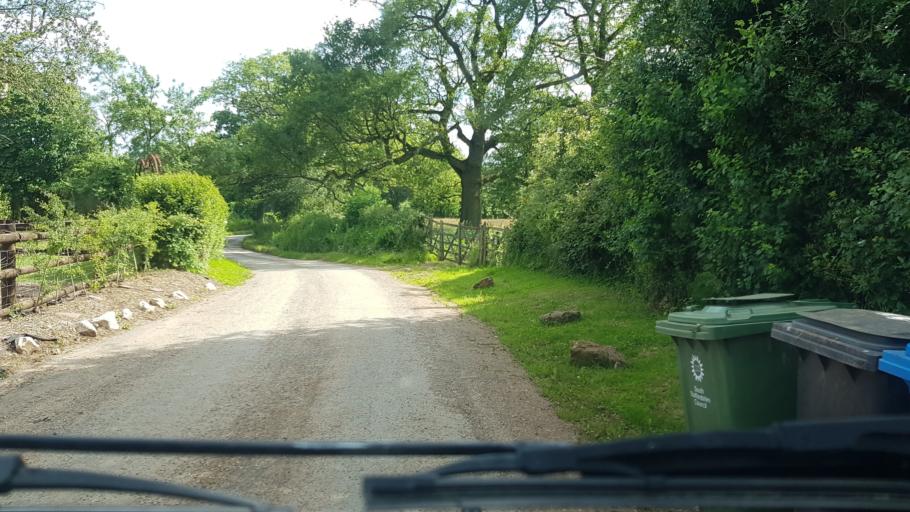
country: GB
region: England
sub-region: Shropshire
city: Romsley
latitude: 52.4585
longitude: -2.2906
